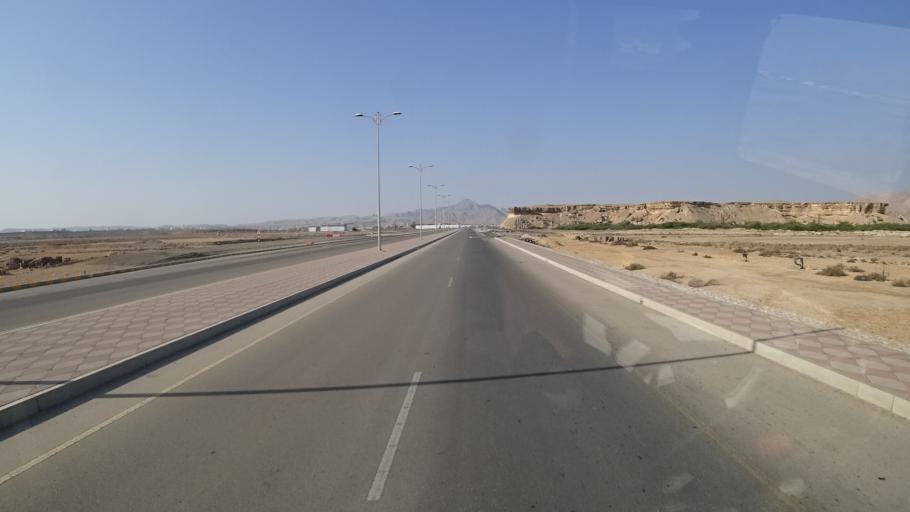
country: OM
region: Ash Sharqiyah
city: Sur
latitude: 22.5963
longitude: 59.4792
